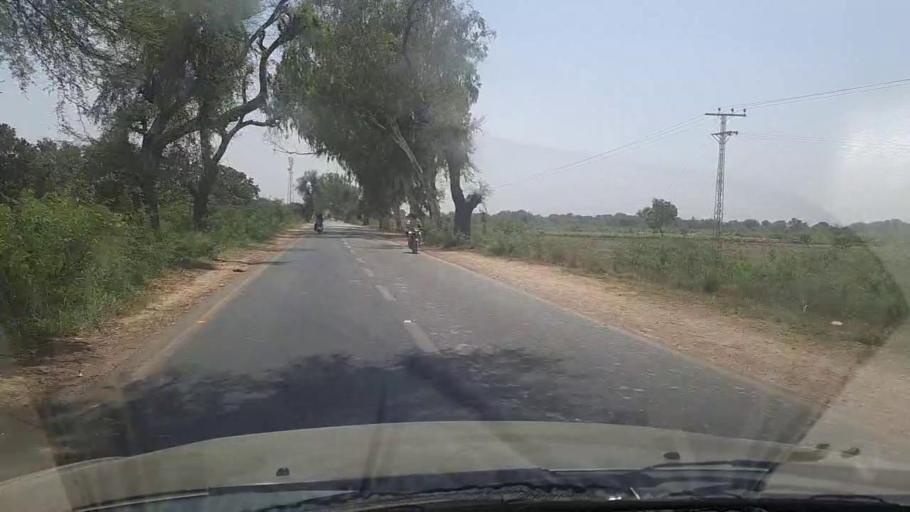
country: PK
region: Sindh
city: Tando Jam
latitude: 25.3231
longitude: 68.5516
